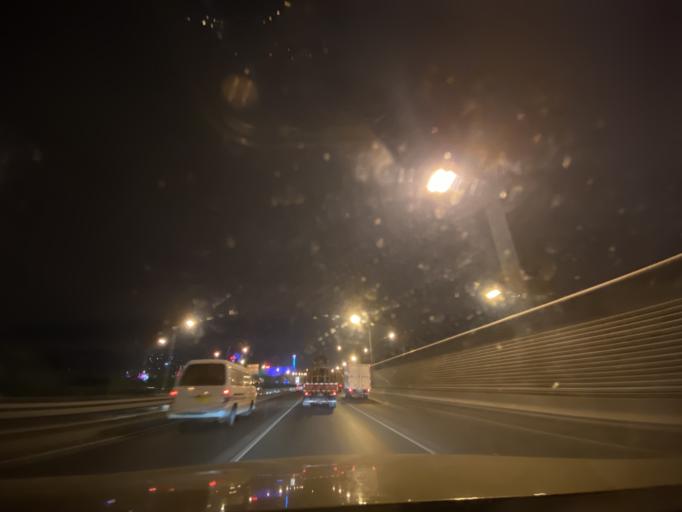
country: CN
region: Beijing
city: Lugu
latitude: 39.9078
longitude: 116.2052
